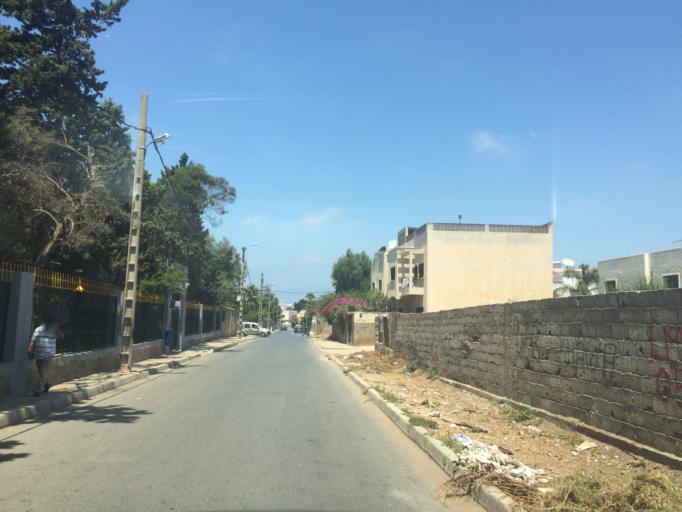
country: MA
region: Rabat-Sale-Zemmour-Zaer
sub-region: Rabat
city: Rabat
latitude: 33.9908
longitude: -6.8230
